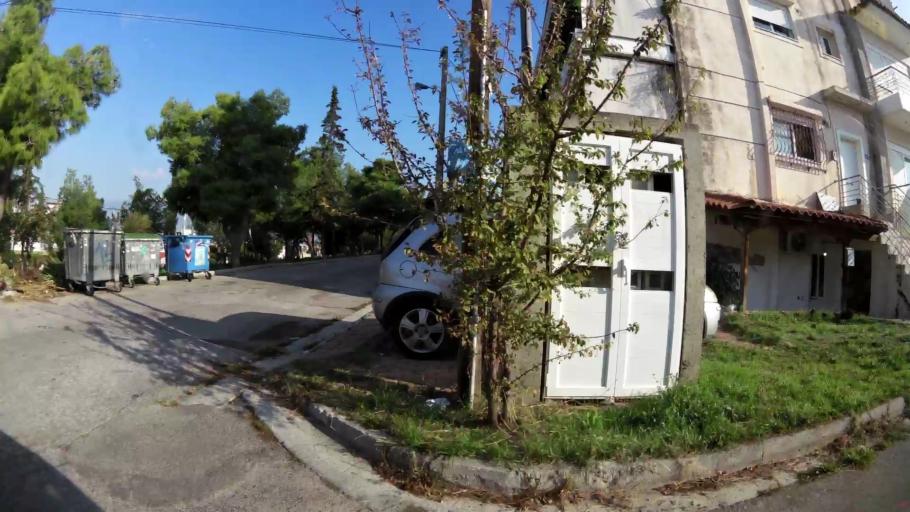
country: GR
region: Attica
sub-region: Nomarchia Dytikis Attikis
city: Zefyri
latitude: 38.0588
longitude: 23.7354
